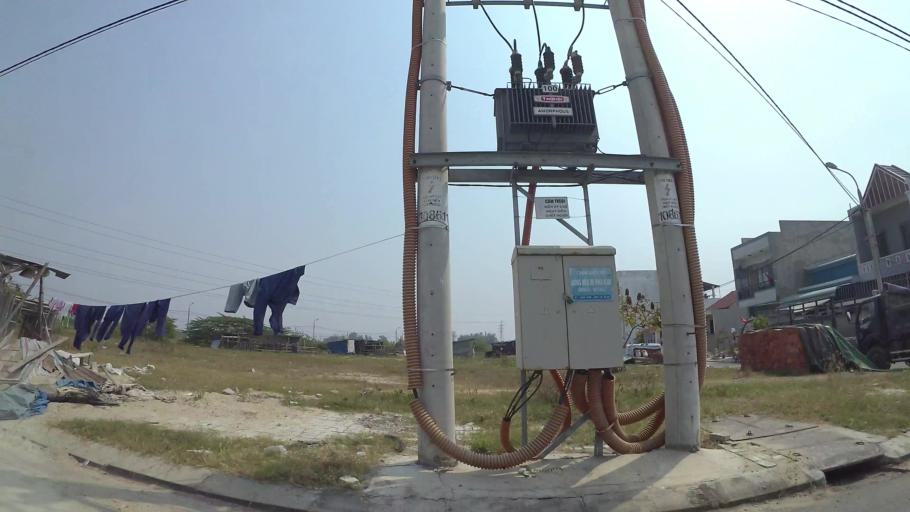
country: VN
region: Da Nang
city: Cam Le
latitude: 15.9690
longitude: 108.2138
